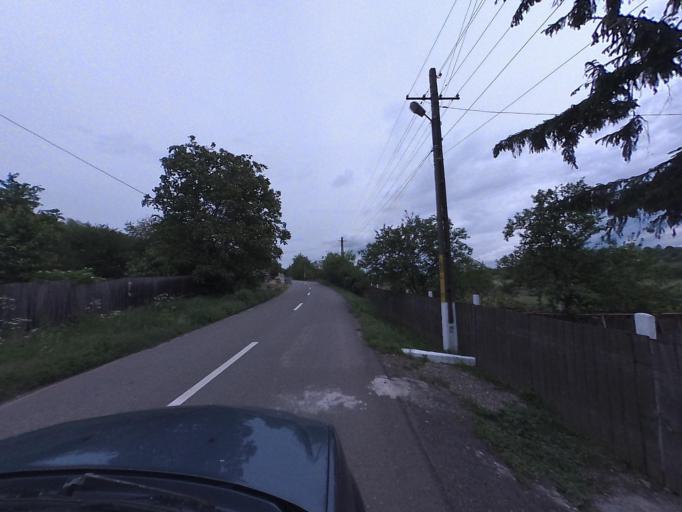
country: RO
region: Neamt
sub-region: Comuna Dulcesti
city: Dulcesti
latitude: 46.9617
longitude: 26.7909
